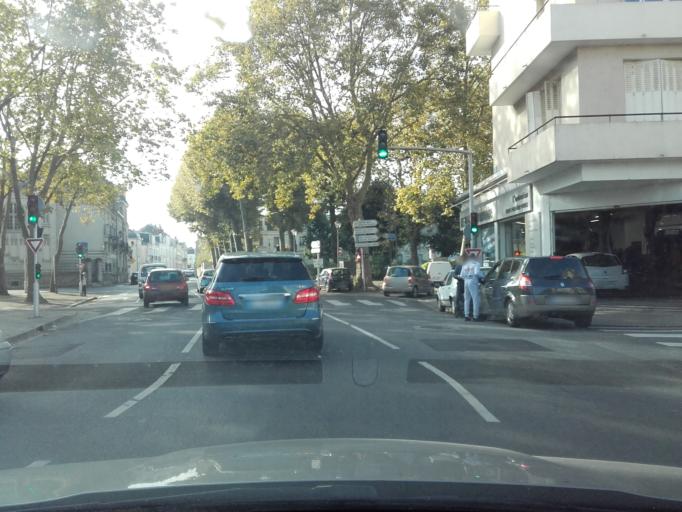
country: FR
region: Centre
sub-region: Departement d'Indre-et-Loire
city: Tours
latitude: 47.3927
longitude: 0.7002
